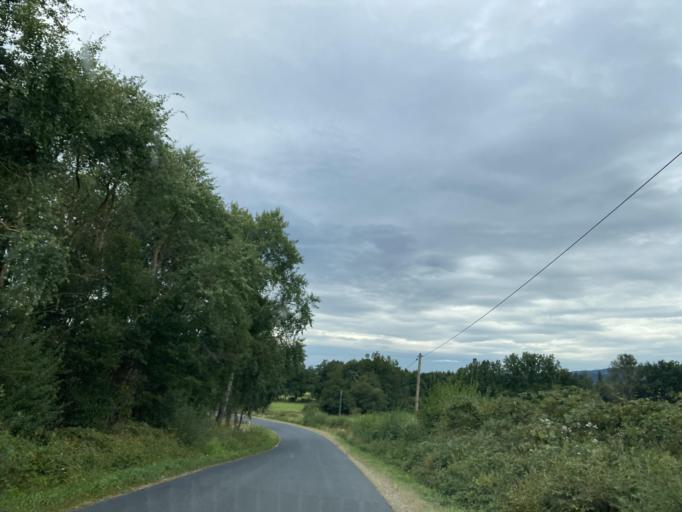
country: FR
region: Auvergne
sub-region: Departement du Puy-de-Dome
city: Marsac-en-Livradois
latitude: 45.5030
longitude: 3.7408
